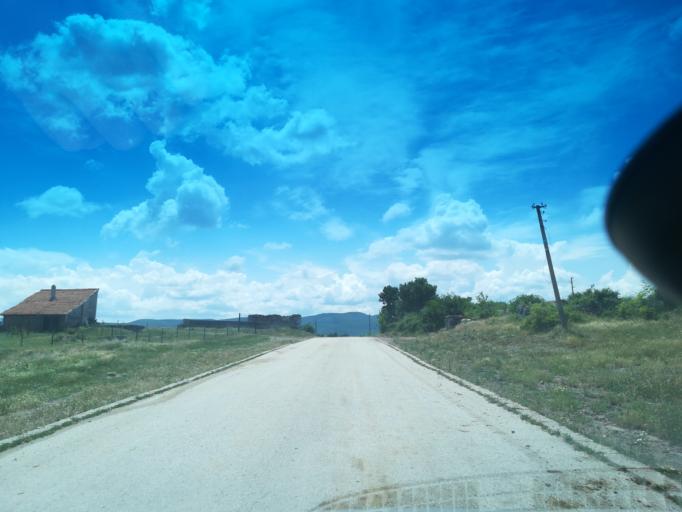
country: BG
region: Khaskovo
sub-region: Obshtina Mineralni Bani
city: Mineralni Bani
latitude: 41.9511
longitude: 25.2482
